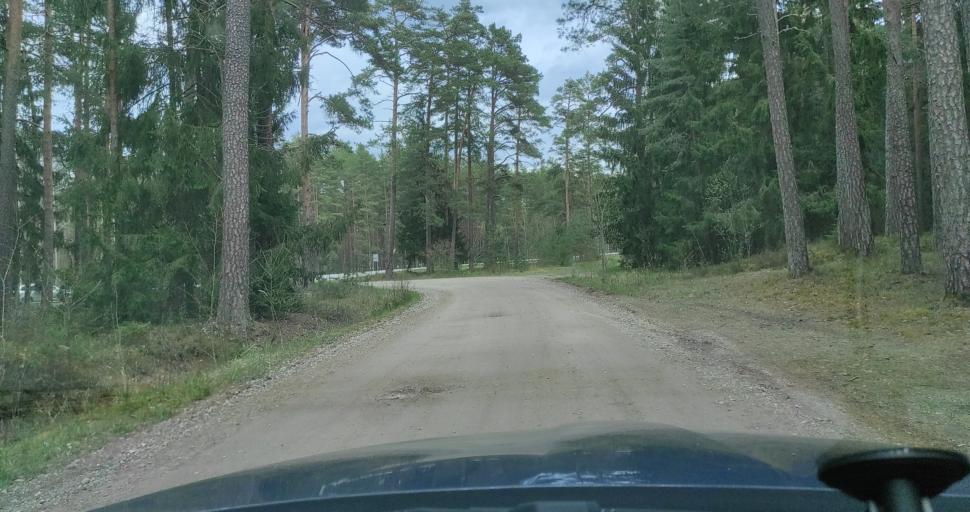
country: LV
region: Talsu Rajons
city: Stende
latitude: 57.2196
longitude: 22.2498
